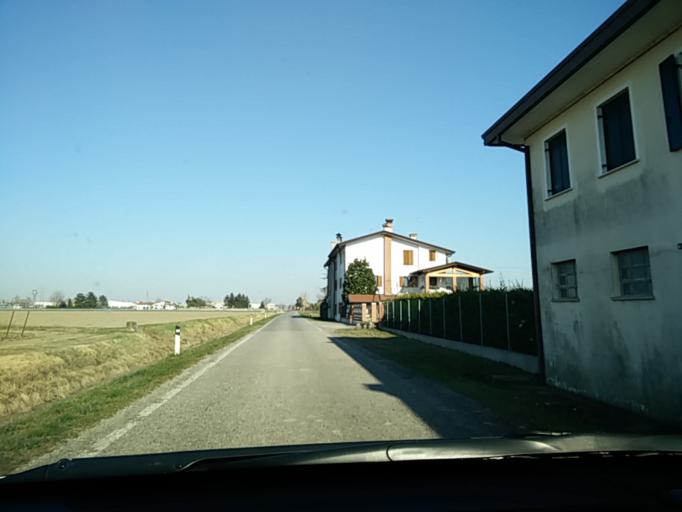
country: IT
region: Veneto
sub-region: Provincia di Venezia
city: Musile di Piave
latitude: 45.6126
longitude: 12.5262
